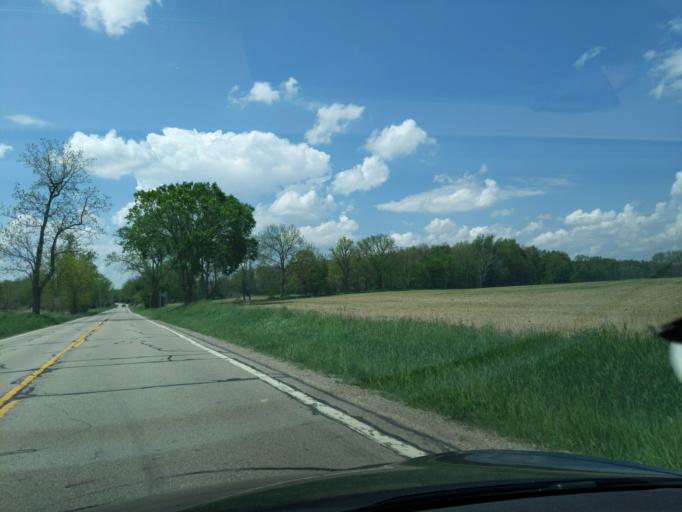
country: US
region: Michigan
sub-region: Ingham County
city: Stockbridge
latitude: 42.4978
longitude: -84.1238
